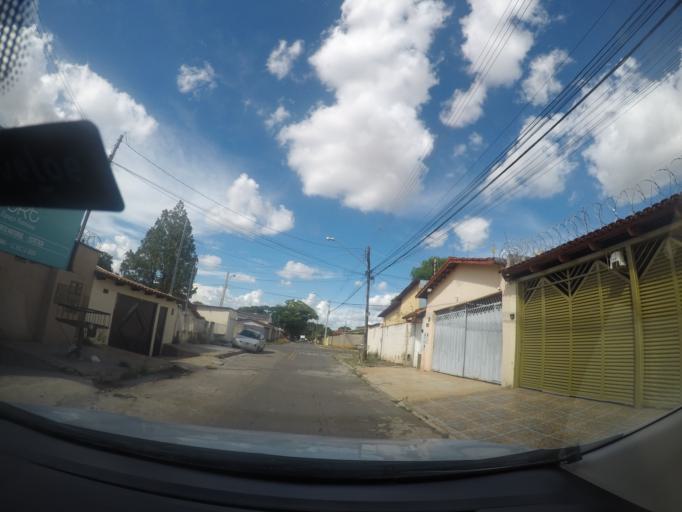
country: BR
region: Goias
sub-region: Goiania
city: Goiania
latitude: -16.6760
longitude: -49.3011
